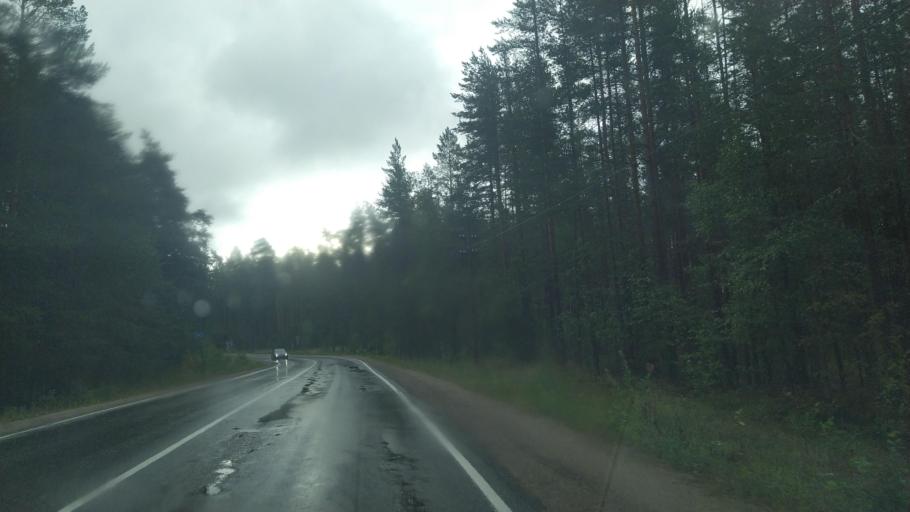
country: RU
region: Leningrad
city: Priozersk
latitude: 61.0017
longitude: 30.1979
